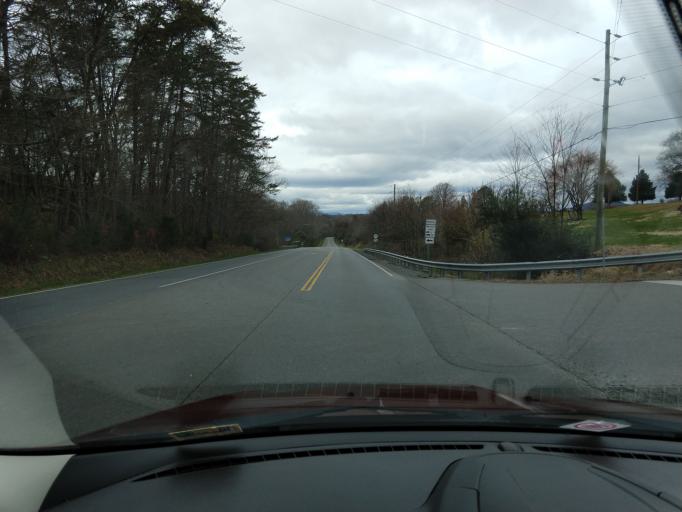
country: US
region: Virginia
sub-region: Botetourt County
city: Blue Ridge
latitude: 37.2599
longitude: -79.7368
